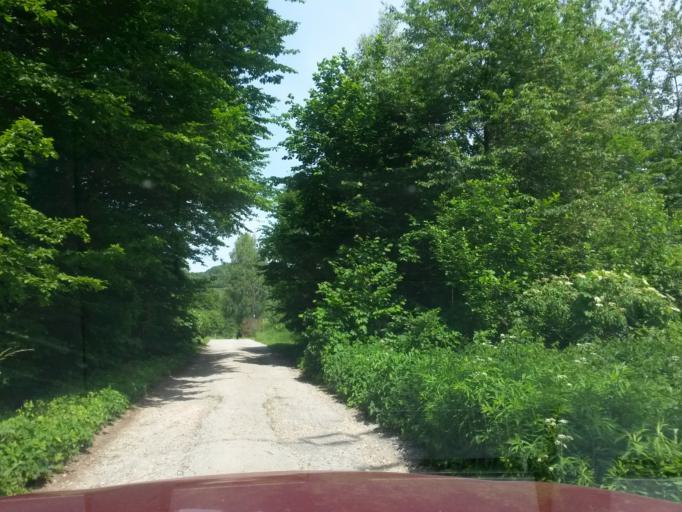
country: SK
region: Kosicky
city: Kosice
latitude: 48.7357
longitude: 21.1192
